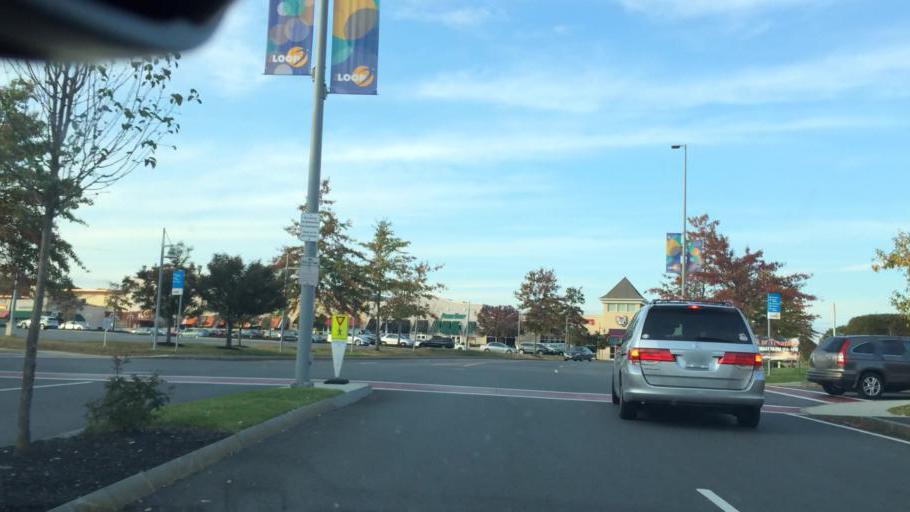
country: US
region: Massachusetts
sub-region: Essex County
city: Lawrence
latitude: 42.7415
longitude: -71.1562
